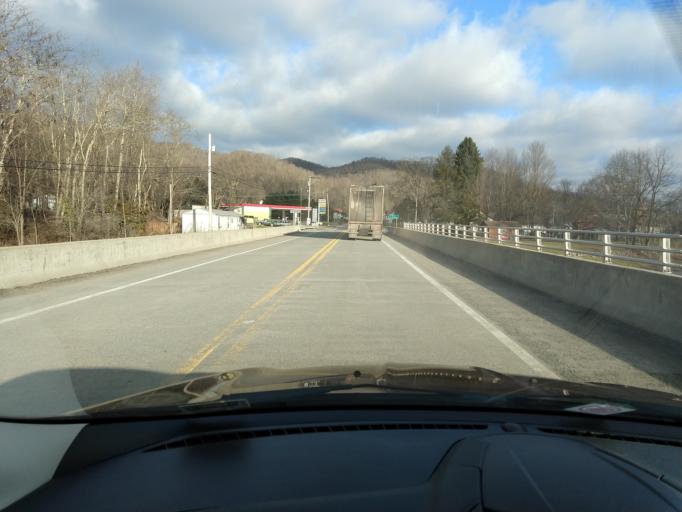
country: US
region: West Virginia
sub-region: Randolph County
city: Elkins
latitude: 38.7092
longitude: -79.9784
